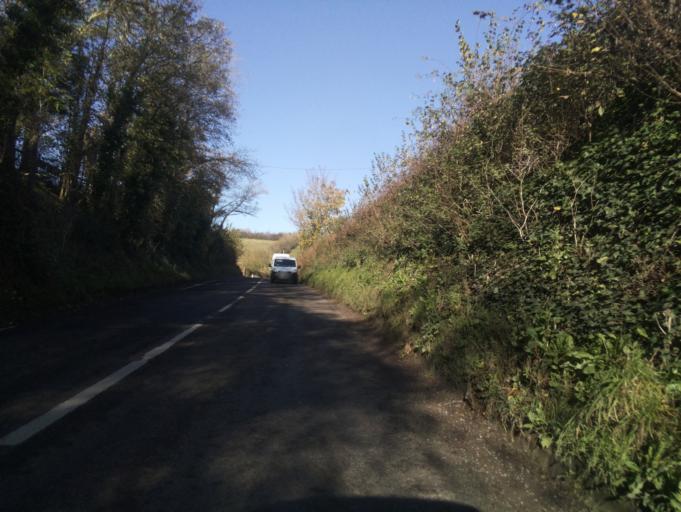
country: GB
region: England
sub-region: Somerset
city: Langport
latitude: 51.0496
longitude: -2.8278
